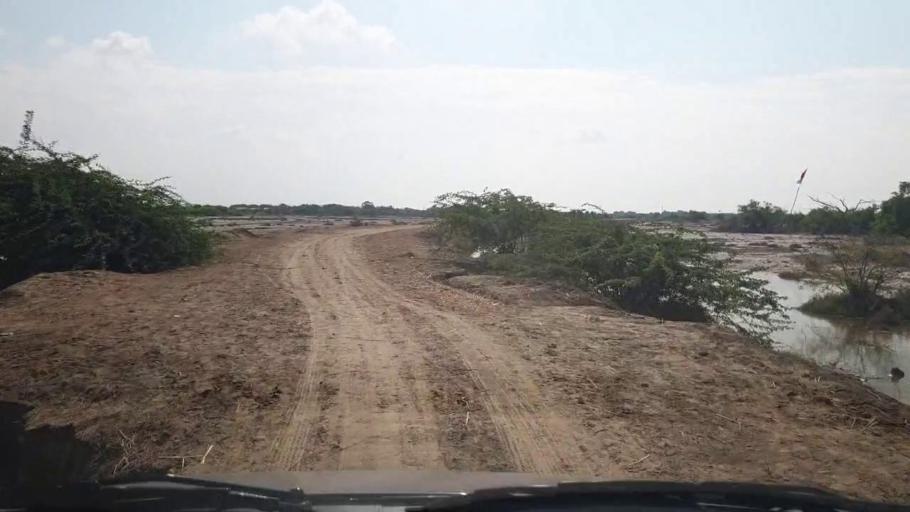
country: PK
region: Sindh
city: Badin
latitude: 24.4834
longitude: 68.6121
